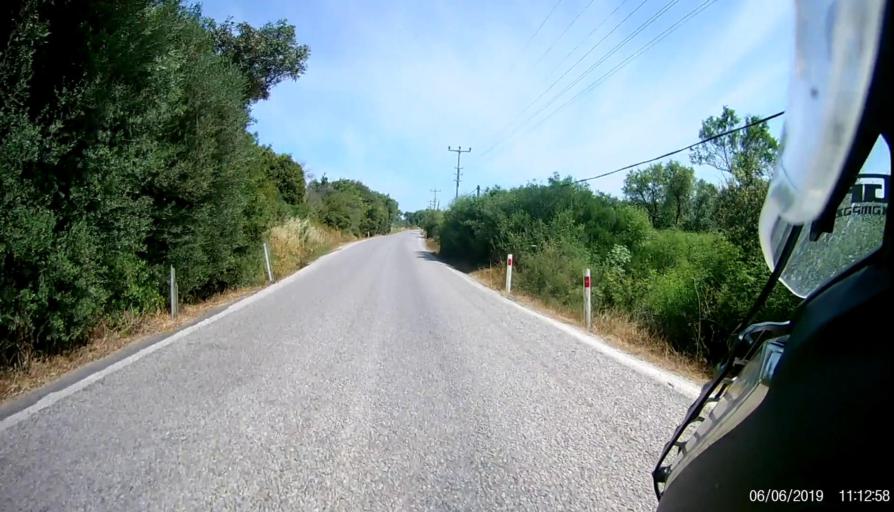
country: TR
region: Canakkale
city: Gulpinar
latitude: 39.6127
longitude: 26.1820
